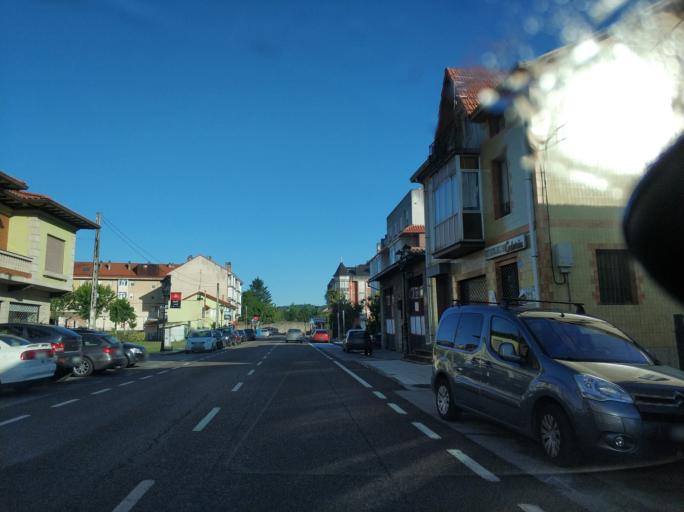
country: ES
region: Cantabria
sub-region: Provincia de Cantabria
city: Puente Viesgo
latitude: 43.3555
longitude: -3.9556
